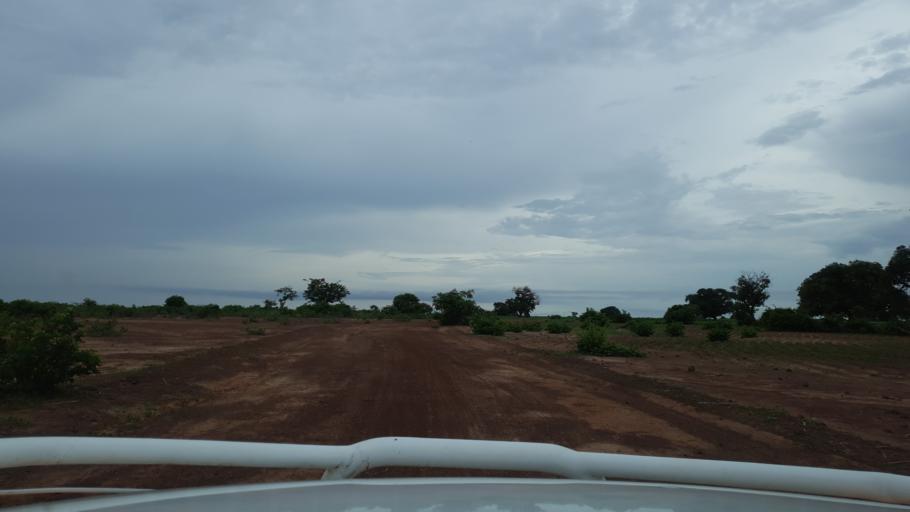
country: ML
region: Segou
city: Bla
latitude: 12.7394
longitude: -5.6506
